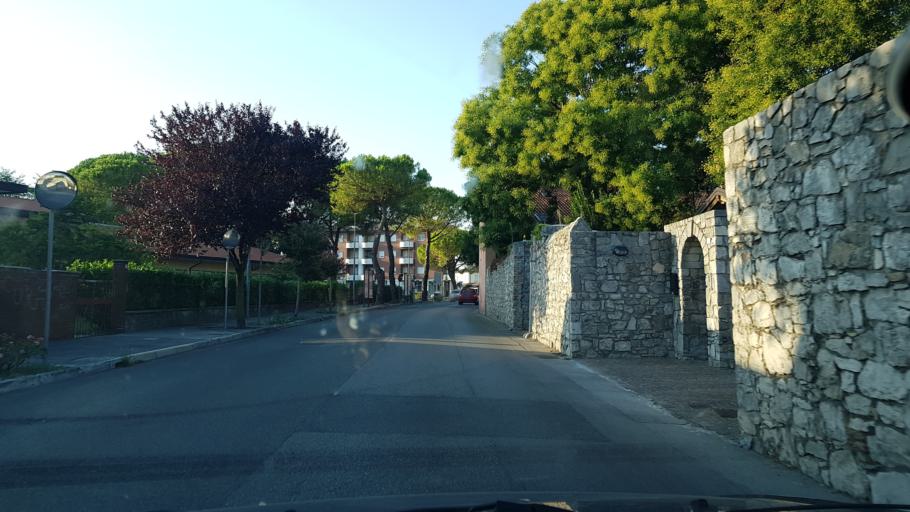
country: IT
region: Friuli Venezia Giulia
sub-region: Provincia di Gorizia
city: Staranzano
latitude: 45.8042
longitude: 13.5057
